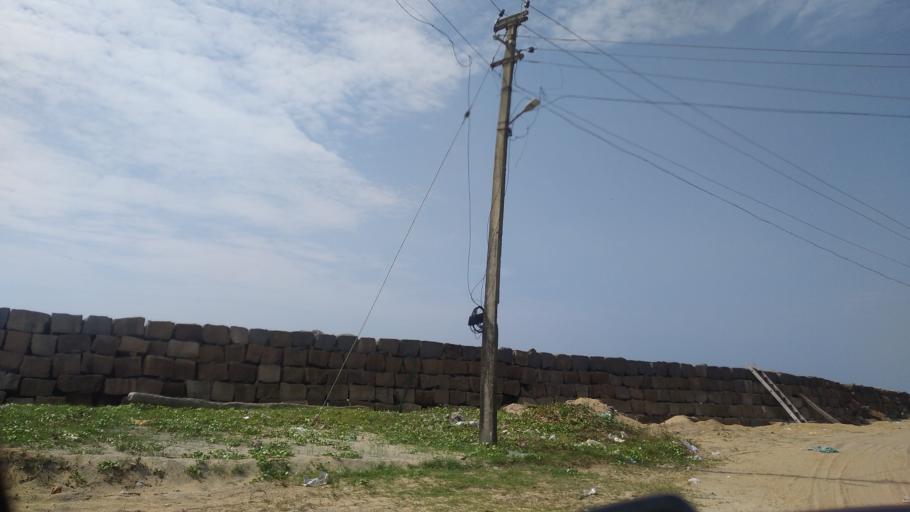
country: IN
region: Kerala
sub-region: Ernakulam
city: Elur
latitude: 10.0853
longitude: 76.1933
